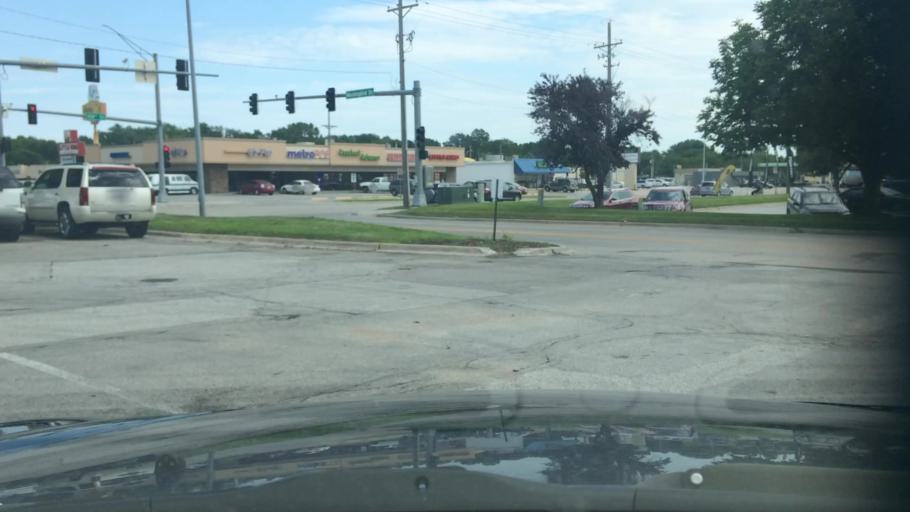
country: US
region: Nebraska
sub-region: Douglas County
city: Ralston
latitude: 41.2082
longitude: -96.0824
